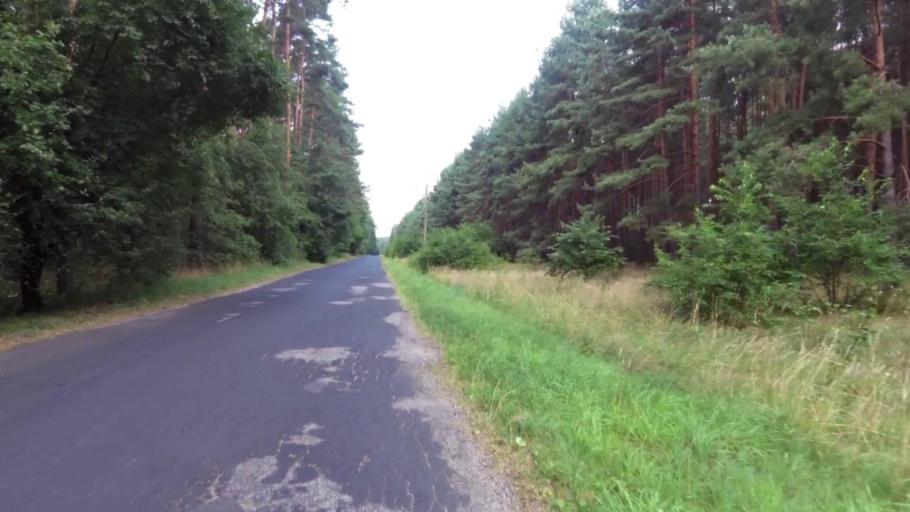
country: PL
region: West Pomeranian Voivodeship
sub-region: Powiat mysliborski
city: Debno
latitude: 52.8488
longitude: 14.7388
